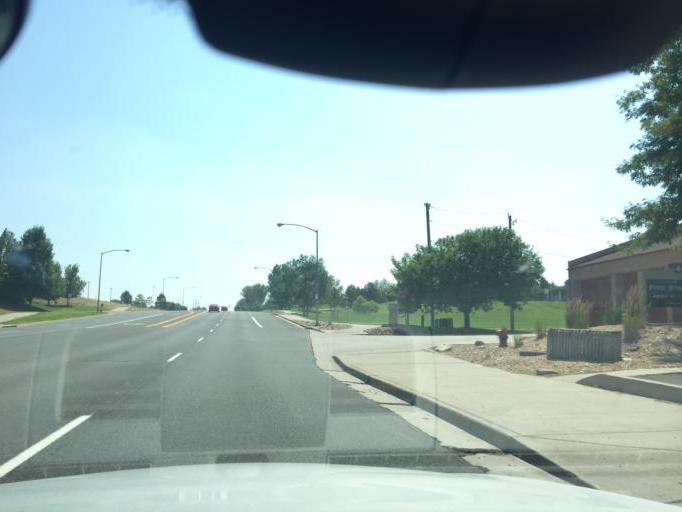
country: US
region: Colorado
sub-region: Broomfield County
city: Broomfield
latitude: 39.8996
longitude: -105.0450
